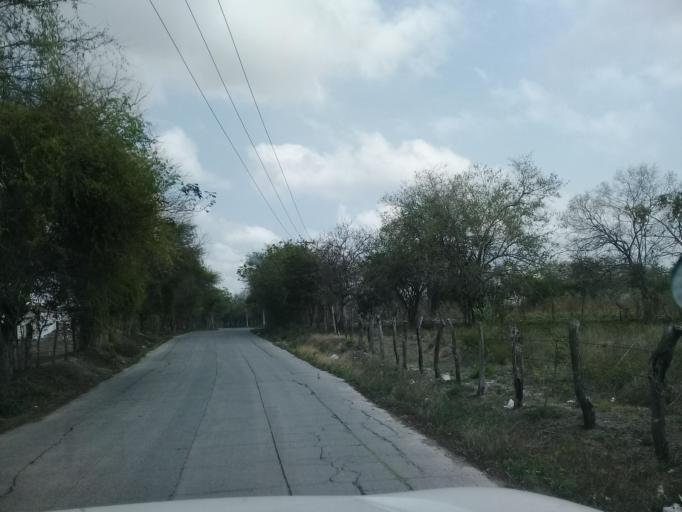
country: MX
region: Veracruz
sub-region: Emiliano Zapata
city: Plan del Rio
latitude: 19.3570
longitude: -96.6532
